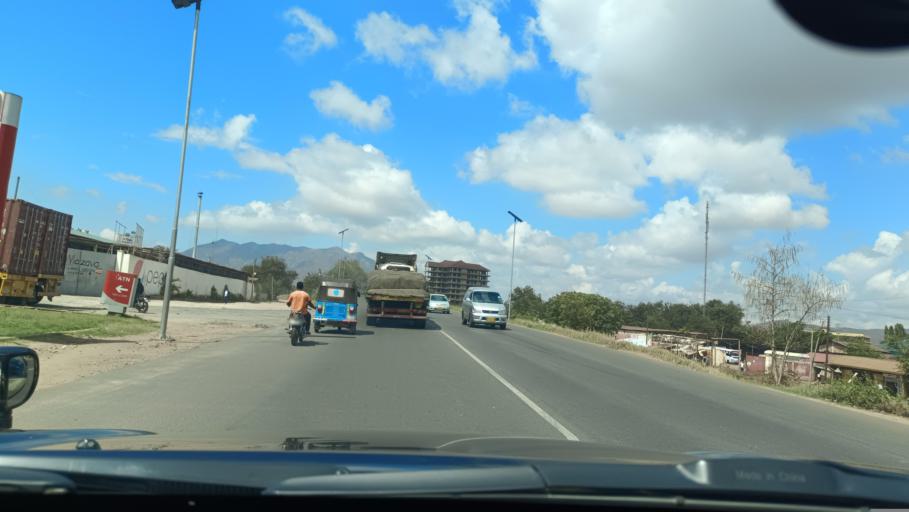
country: TZ
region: Morogoro
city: Morogoro
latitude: -6.8057
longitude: 37.6593
